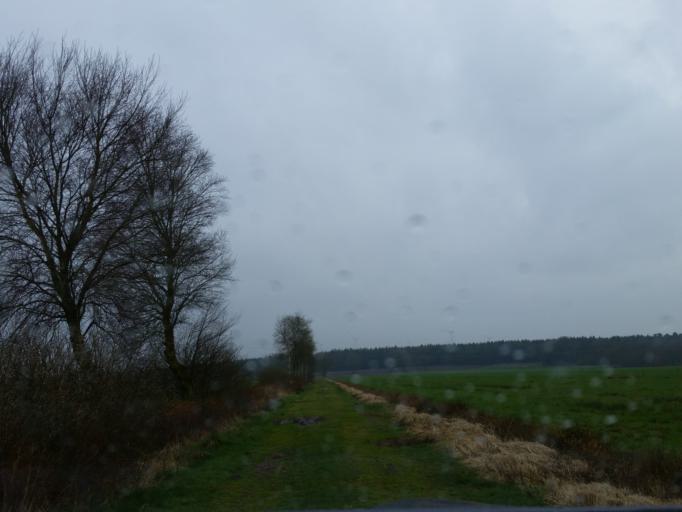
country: DE
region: Lower Saxony
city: Stinstedt
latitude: 53.5985
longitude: 8.9748
